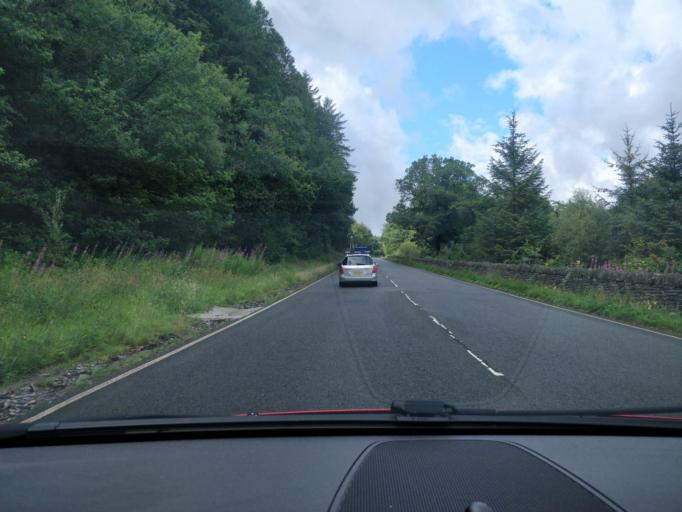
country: GB
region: Wales
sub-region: Gwynedd
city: Blaenau-Ffestiniog
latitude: 53.0429
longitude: -3.9172
